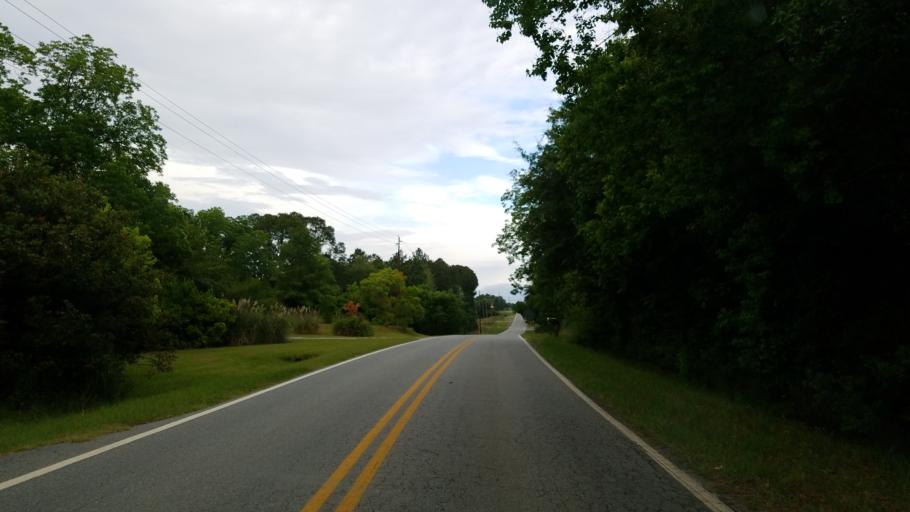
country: US
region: Georgia
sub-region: Tift County
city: Tifton
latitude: 31.5486
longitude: -83.5397
